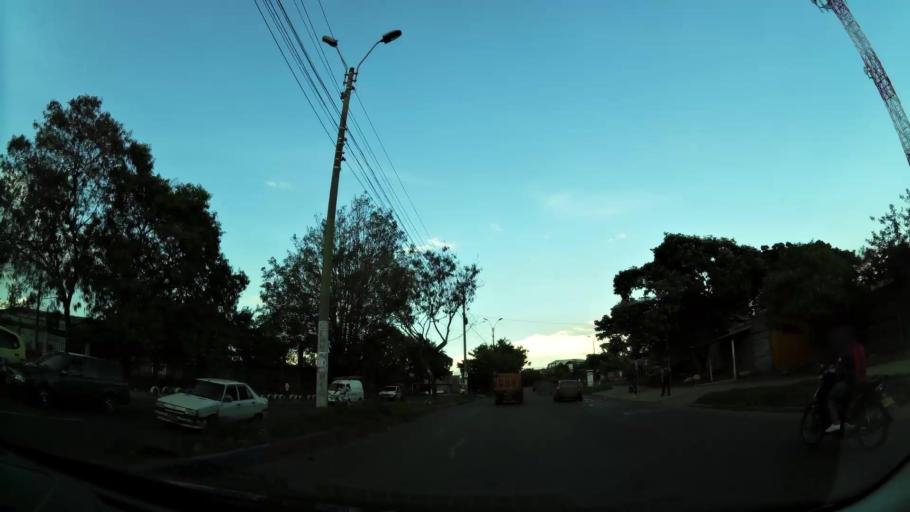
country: CO
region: Valle del Cauca
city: Cali
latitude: 3.4080
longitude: -76.4968
